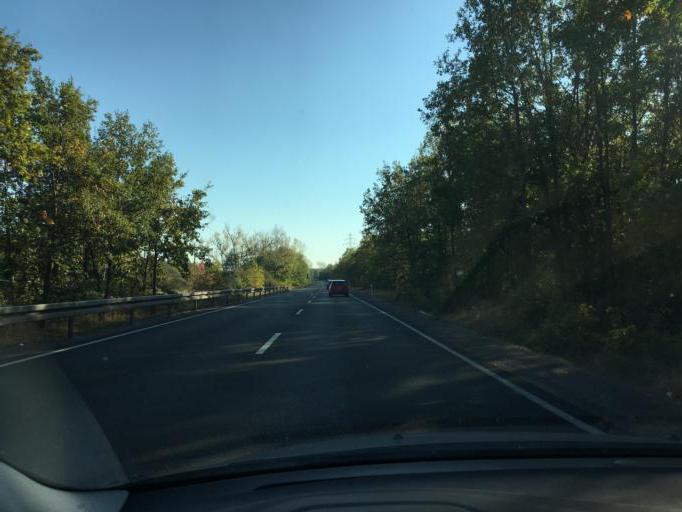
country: DE
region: Saxony-Anhalt
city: Roitzsch
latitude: 51.5775
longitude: 12.2844
